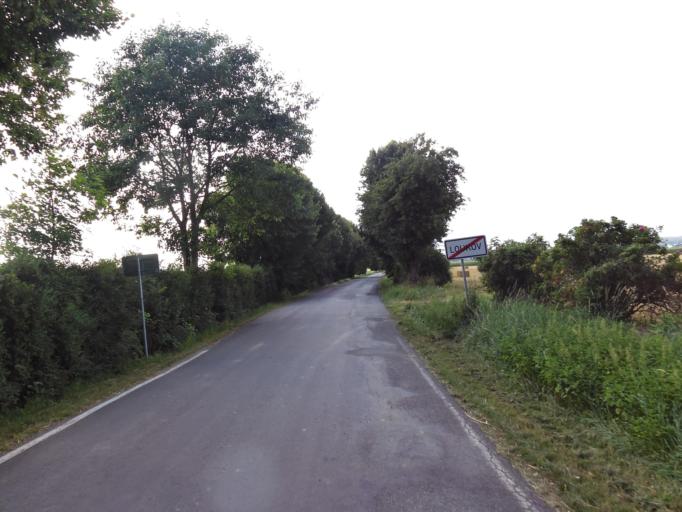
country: CZ
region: Central Bohemia
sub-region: Okres Mlada Boleslav
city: Zd'ar
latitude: 50.5636
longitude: 15.0337
